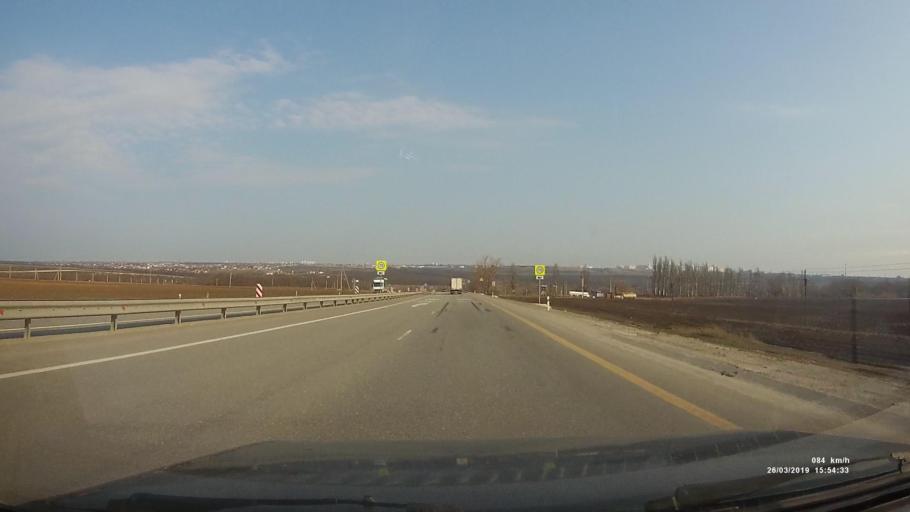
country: RU
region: Rostov
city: Krym
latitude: 47.2688
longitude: 39.5601
